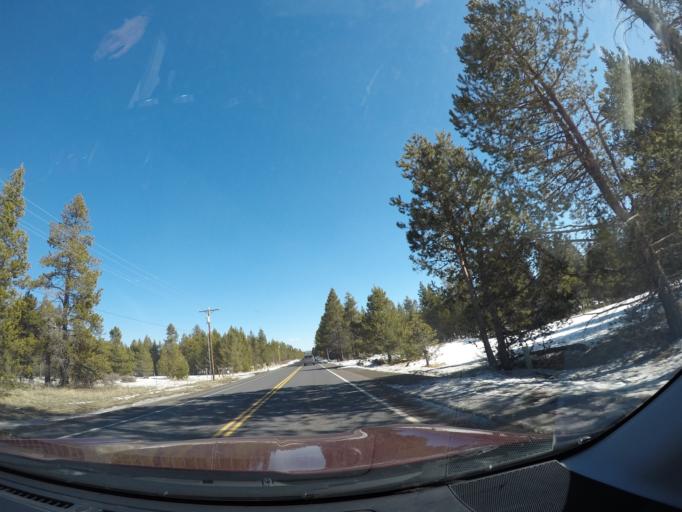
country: US
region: Oregon
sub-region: Deschutes County
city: Sunriver
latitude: 43.8629
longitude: -121.4695
